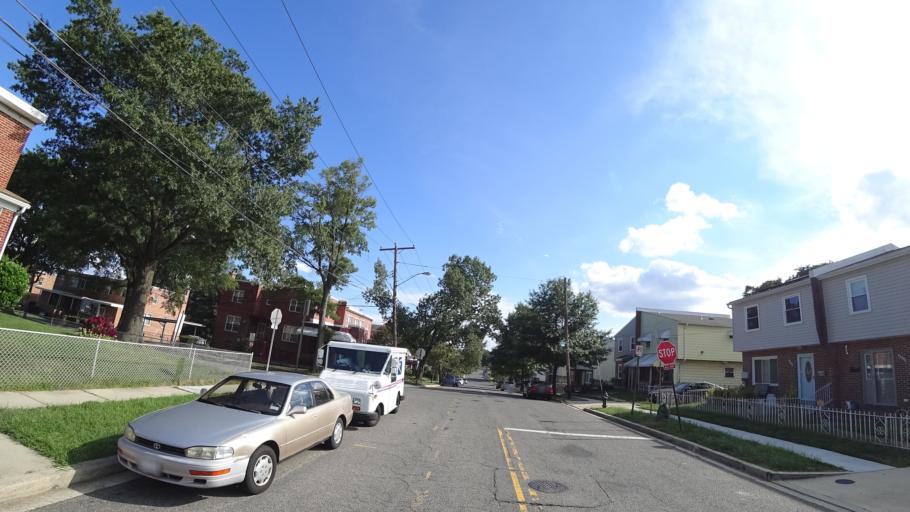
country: US
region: Maryland
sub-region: Prince George's County
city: Chillum
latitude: 38.9475
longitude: -76.9971
